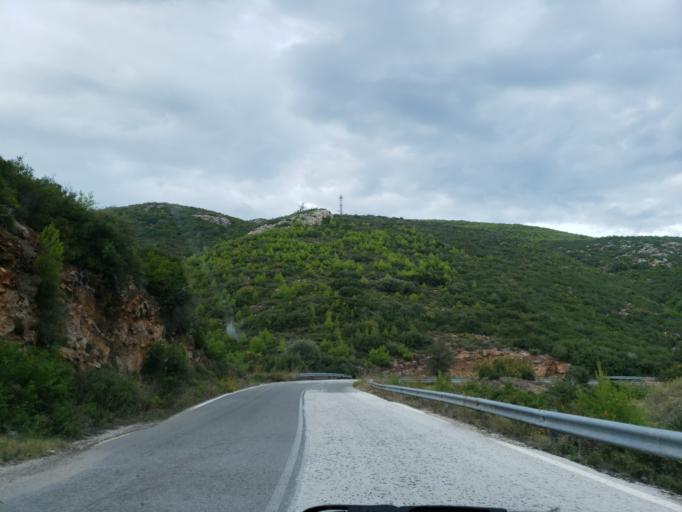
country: GR
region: Attica
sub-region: Nomarchia Anatolikis Attikis
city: Grammatiko
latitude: 38.2107
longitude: 23.9464
